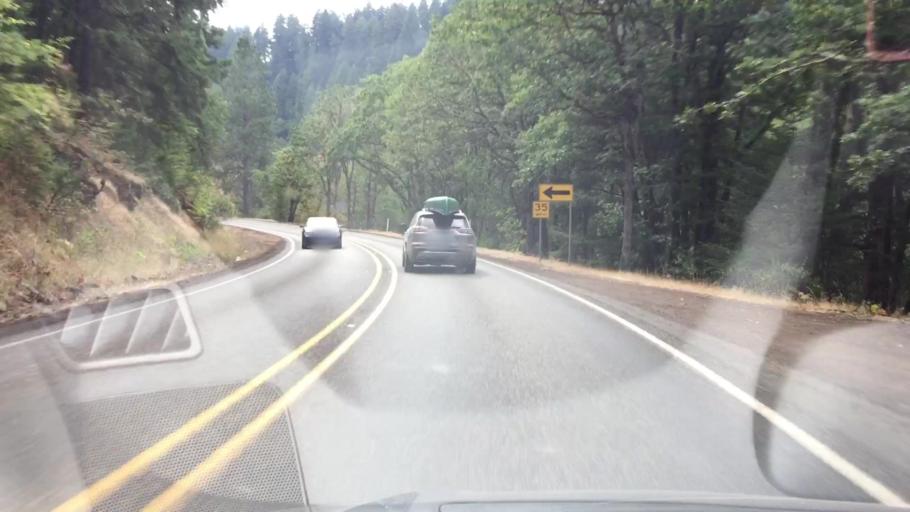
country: US
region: Washington
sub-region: Klickitat County
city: White Salmon
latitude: 45.7463
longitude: -121.5213
